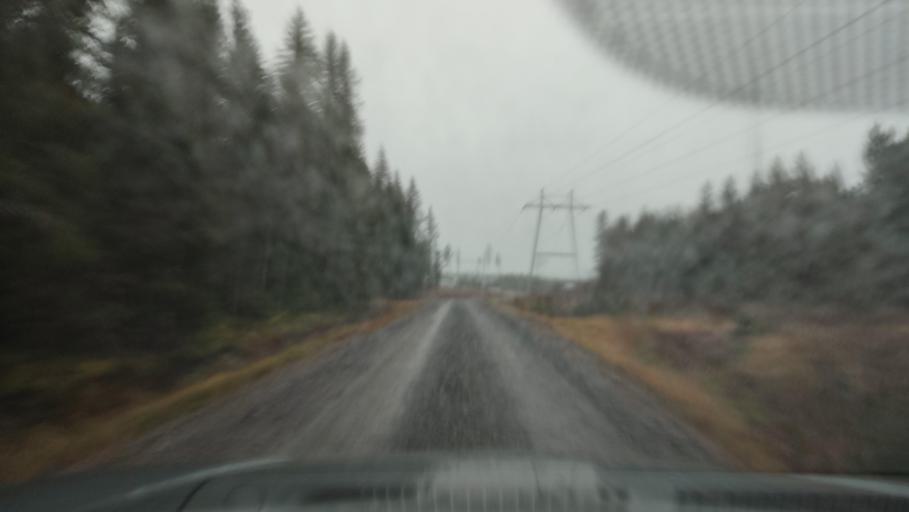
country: FI
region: Southern Ostrobothnia
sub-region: Suupohja
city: Karijoki
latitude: 62.2107
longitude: 21.7297
